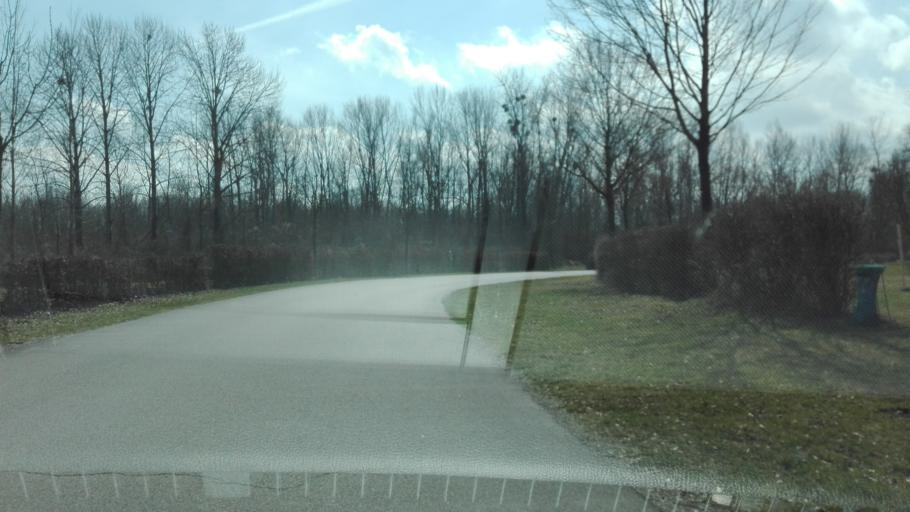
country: AT
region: Upper Austria
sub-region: Politischer Bezirk Urfahr-Umgebung
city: Goldworth
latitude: 48.3240
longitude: 14.0750
